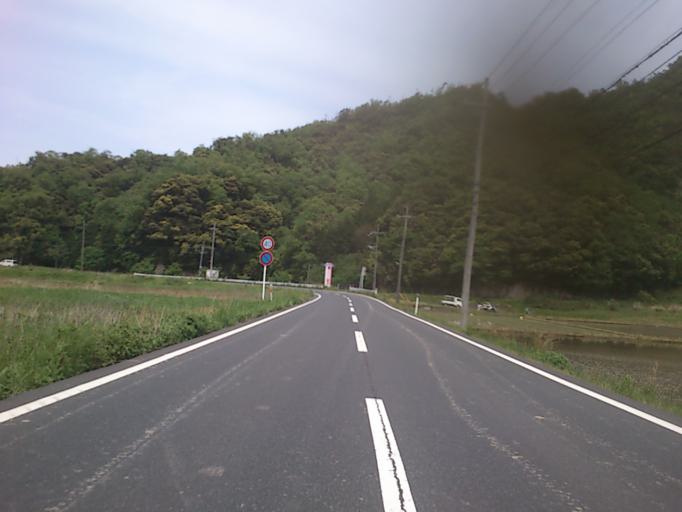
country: JP
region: Kyoto
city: Miyazu
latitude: 35.6964
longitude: 135.1033
